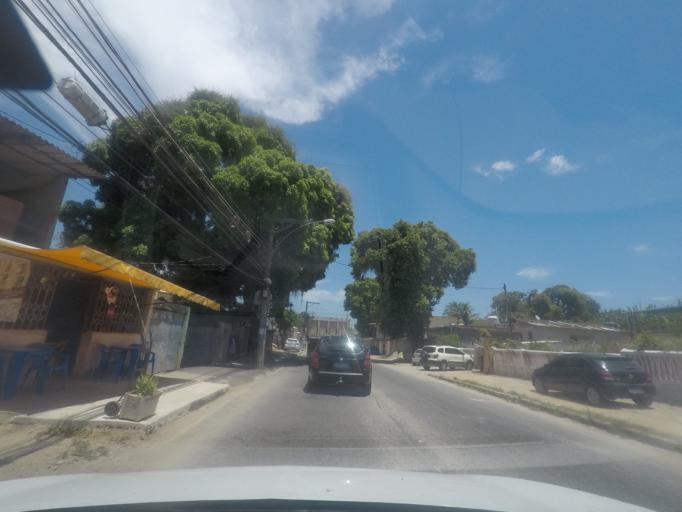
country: BR
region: Rio de Janeiro
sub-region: Itaguai
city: Itaguai
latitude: -22.9329
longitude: -43.6903
